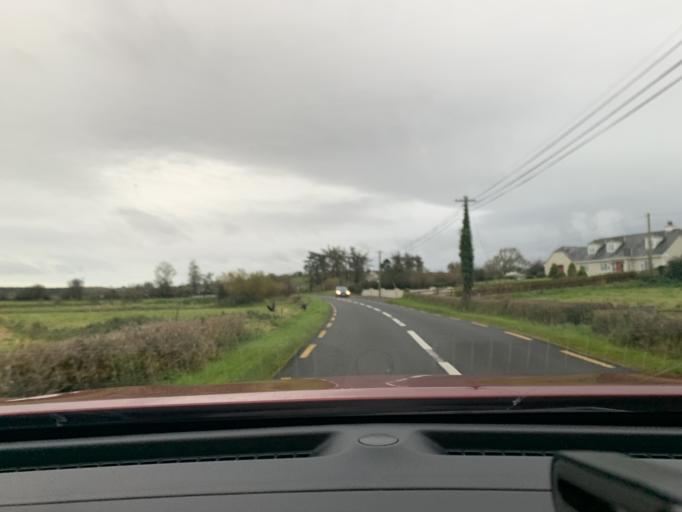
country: IE
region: Connaught
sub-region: Sligo
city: Ballymote
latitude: 54.0540
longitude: -8.5219
